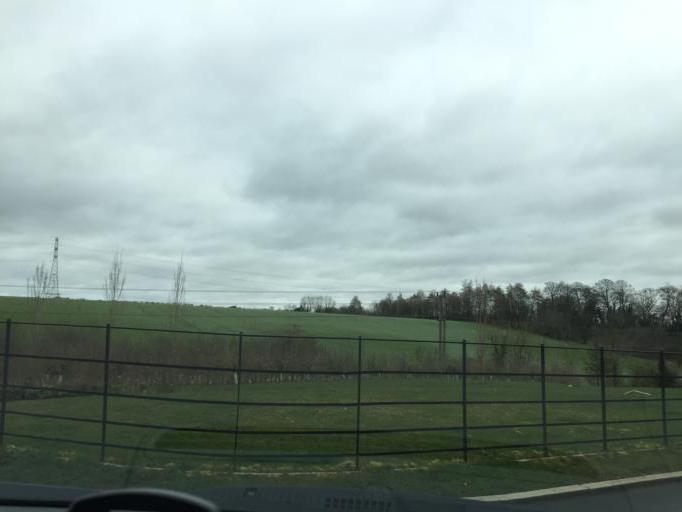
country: GB
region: England
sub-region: Northamptonshire
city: Brackley
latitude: 52.0432
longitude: -1.1373
